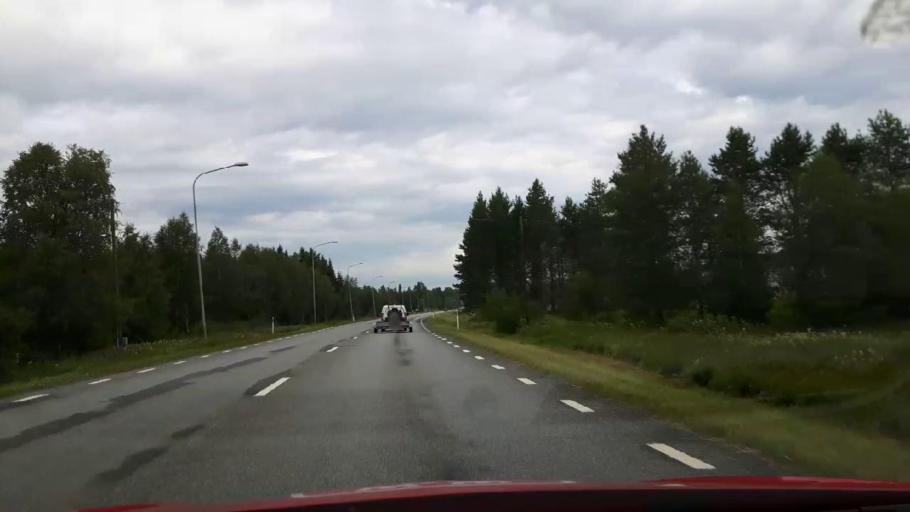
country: SE
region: Jaemtland
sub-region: Stroemsunds Kommun
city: Stroemsund
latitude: 63.6729
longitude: 15.3931
